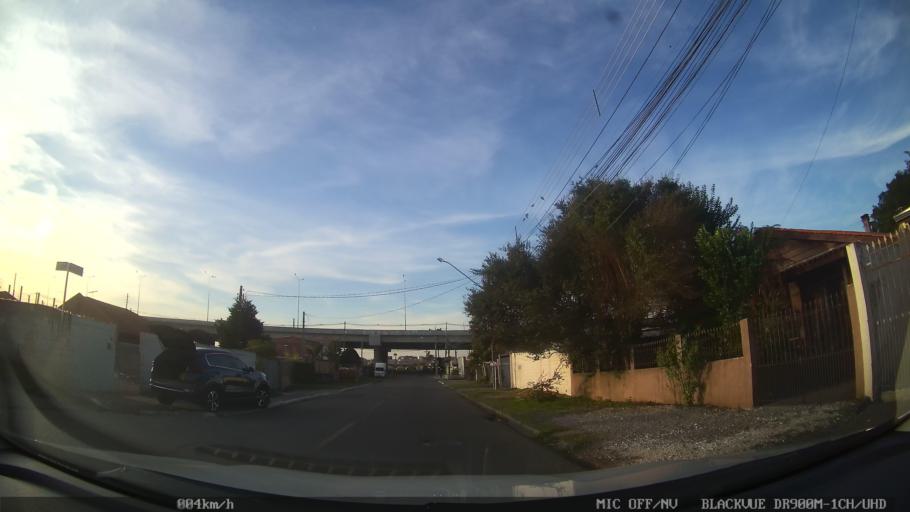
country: BR
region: Parana
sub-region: Pinhais
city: Pinhais
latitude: -25.4393
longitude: -49.1620
